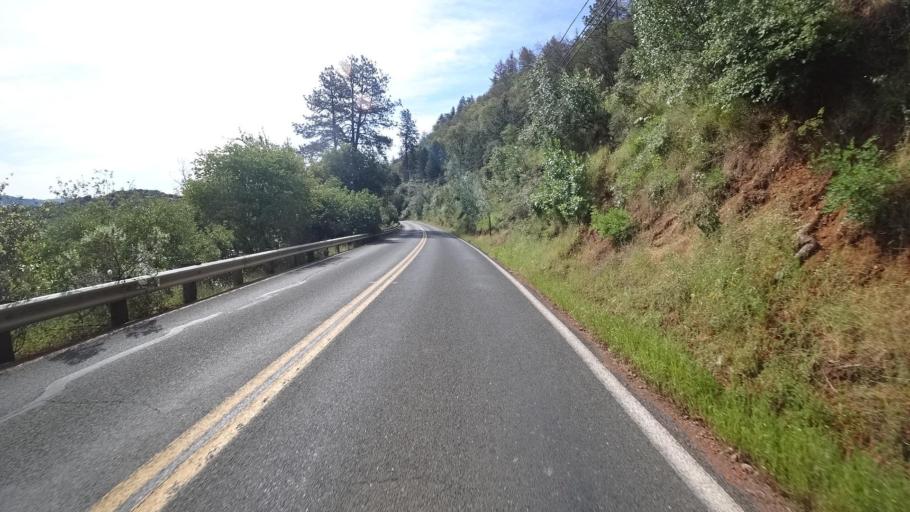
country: US
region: California
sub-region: Lake County
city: Soda Bay
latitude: 39.0064
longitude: -122.7695
